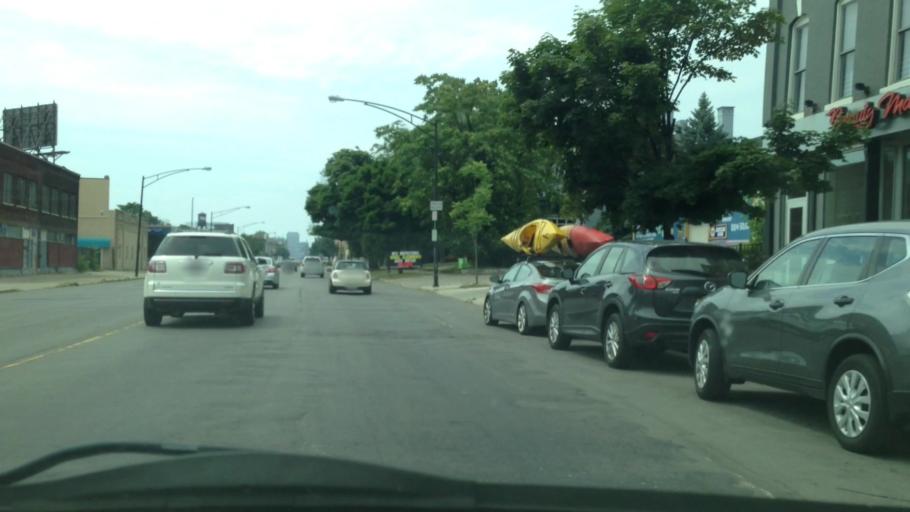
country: US
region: New York
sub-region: Erie County
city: Buffalo
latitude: 42.9151
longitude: -78.8646
